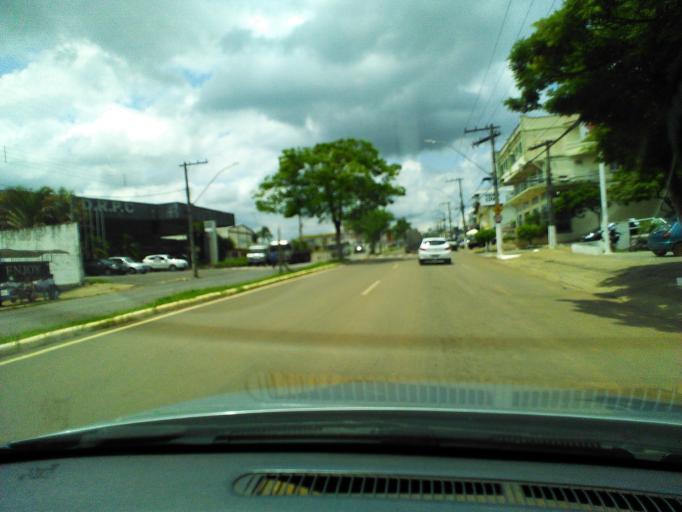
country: BR
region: Minas Gerais
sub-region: Tres Coracoes
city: Tres Coracoes
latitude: -21.6784
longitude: -45.2681
